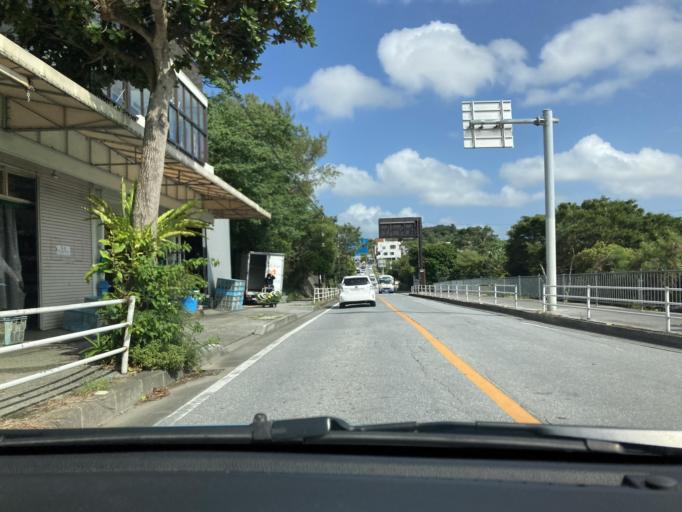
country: JP
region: Okinawa
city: Chatan
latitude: 26.2926
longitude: 127.7846
